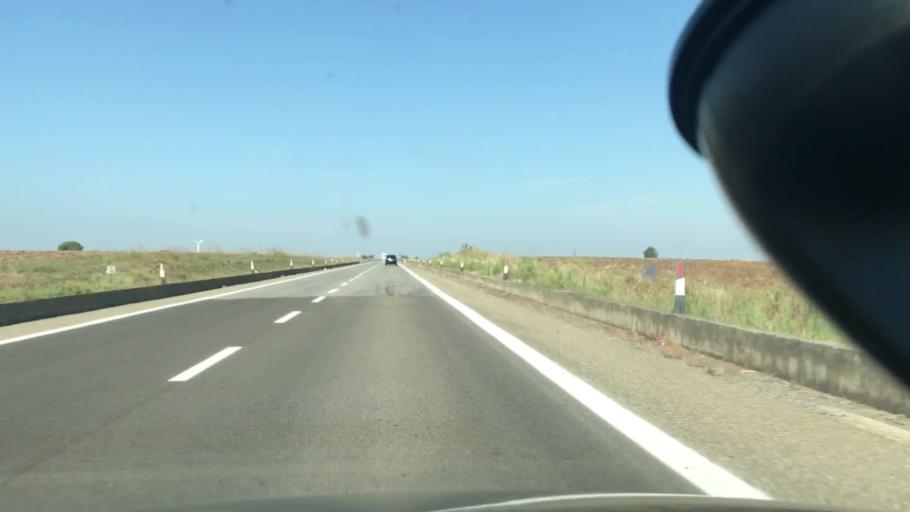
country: IT
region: Basilicate
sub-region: Provincia di Potenza
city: Montemilone
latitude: 40.9891
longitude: 15.9041
